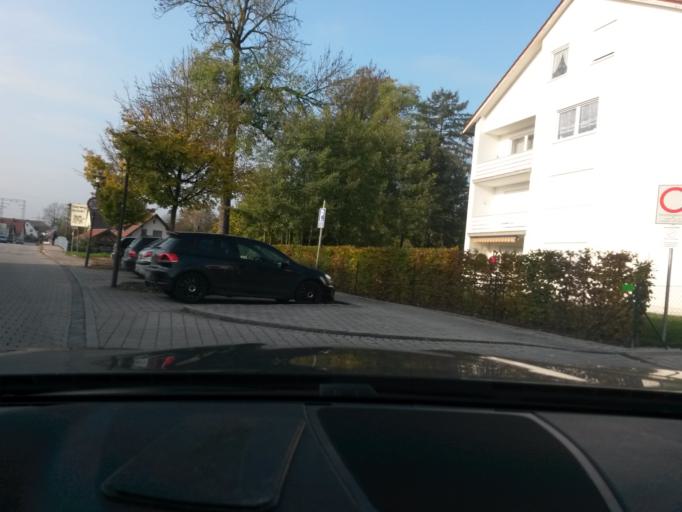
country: DE
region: Bavaria
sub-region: Lower Bavaria
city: Tiefenbach
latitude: 48.5558
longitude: 12.1089
